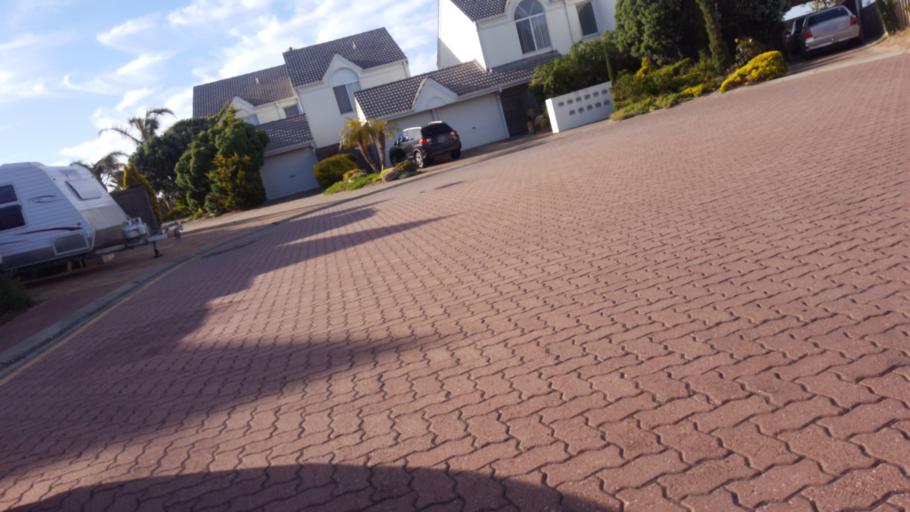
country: AU
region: South Australia
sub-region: Port Adelaide Enfield
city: Birkenhead
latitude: -34.7829
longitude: 138.4807
